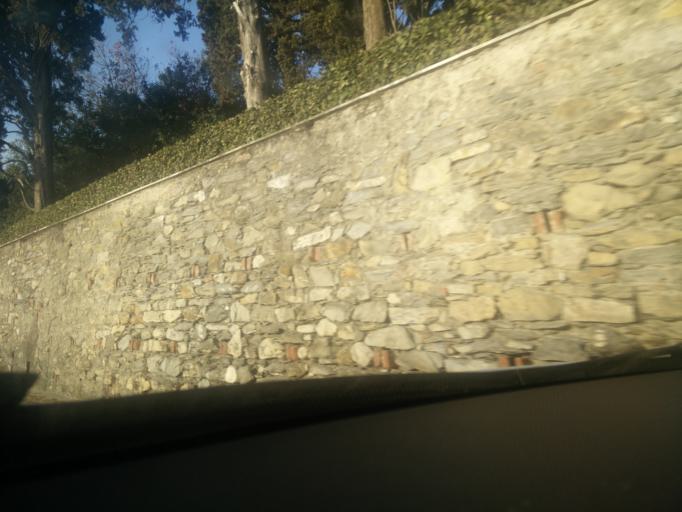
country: IT
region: Tuscany
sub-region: Provincia di Massa-Carrara
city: Carrara
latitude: 44.0576
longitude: 10.0762
